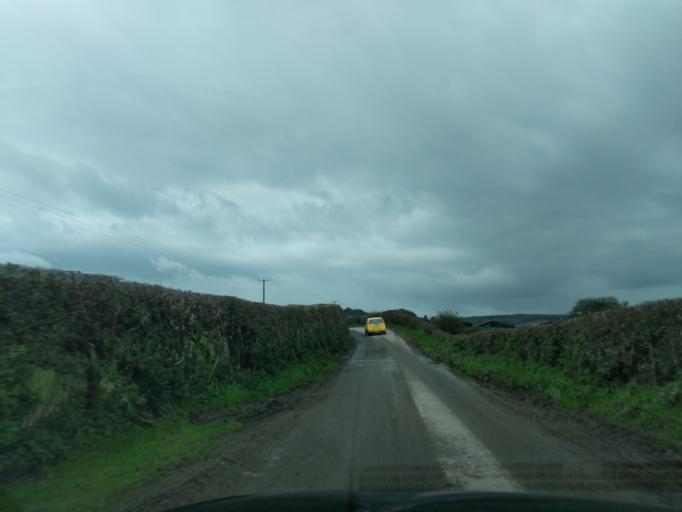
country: GB
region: Scotland
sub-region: Dumfries and Galloway
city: Kirkcudbright
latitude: 54.8934
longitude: -3.9934
